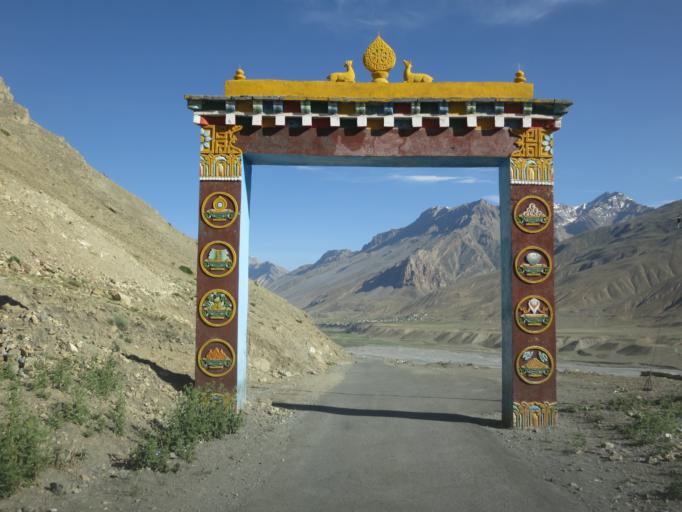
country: IN
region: Himachal Pradesh
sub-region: Shimla
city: Sarahan
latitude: 32.2910
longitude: 78.0138
